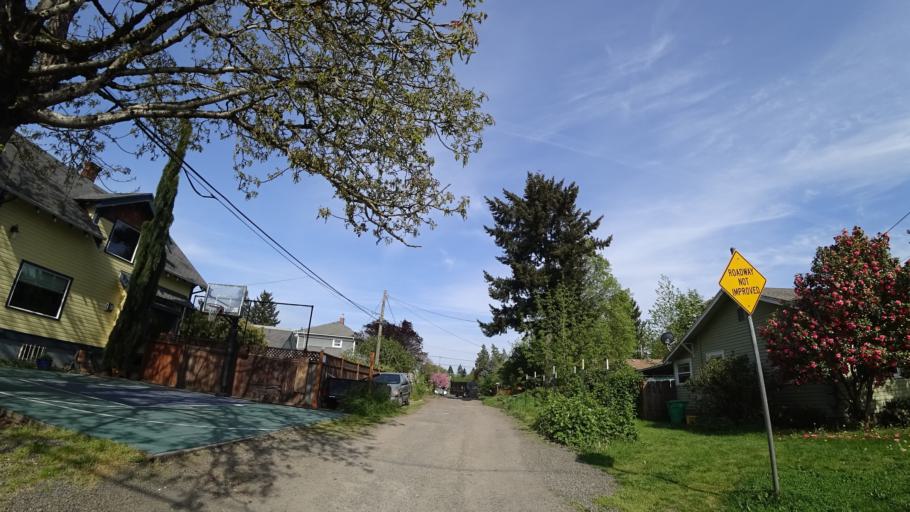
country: US
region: Oregon
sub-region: Clackamas County
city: Milwaukie
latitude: 45.4784
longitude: -122.6124
